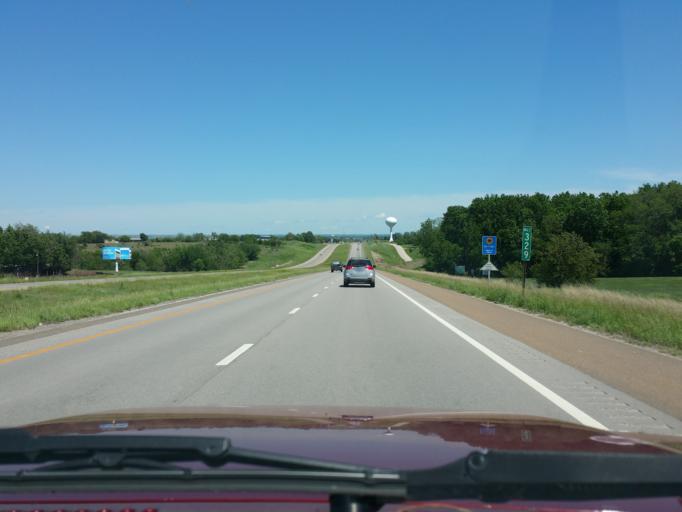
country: US
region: Kansas
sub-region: Pottawatomie County
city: Wamego
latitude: 39.2101
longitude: -96.3417
